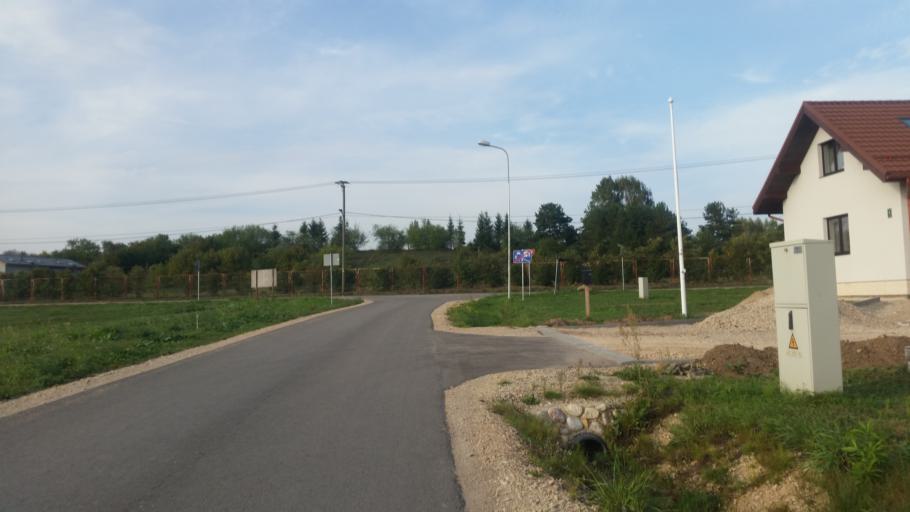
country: LV
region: Ikskile
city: Ikskile
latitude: 56.8187
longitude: 24.5116
